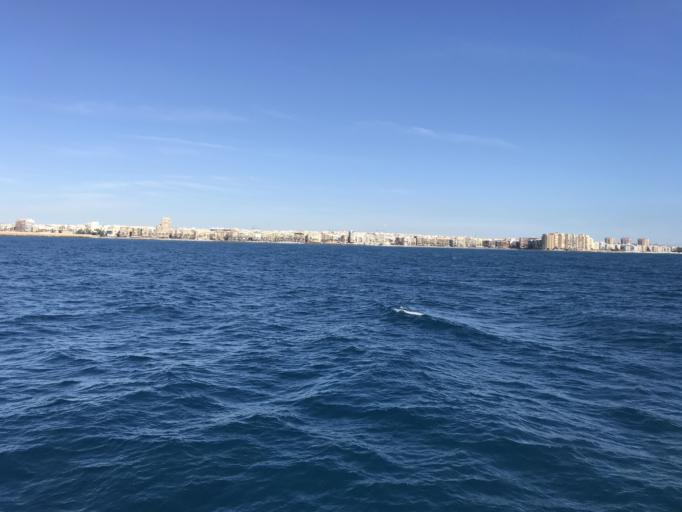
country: ES
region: Valencia
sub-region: Provincia de Alicante
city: Torrevieja
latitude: 37.9640
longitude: -0.6707
